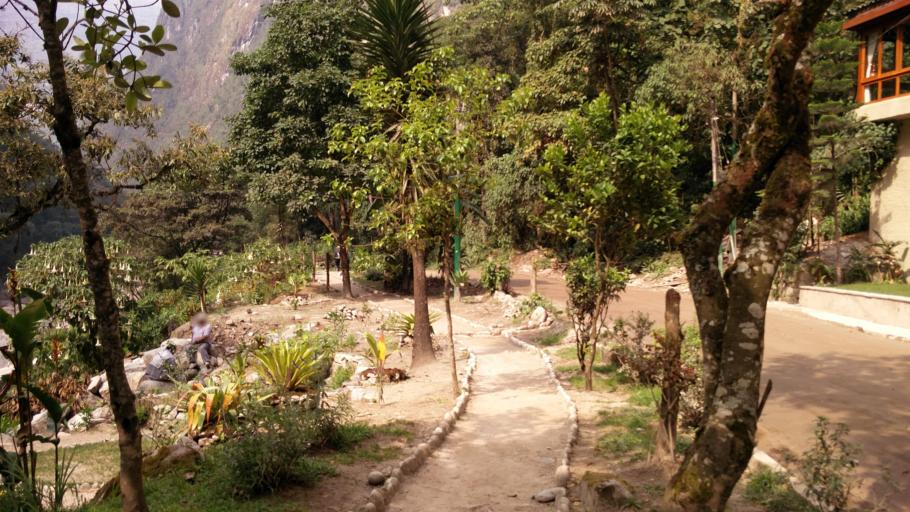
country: PE
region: Cusco
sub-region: Provincia de La Convencion
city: Santa Teresa
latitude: -13.1544
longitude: -72.5282
